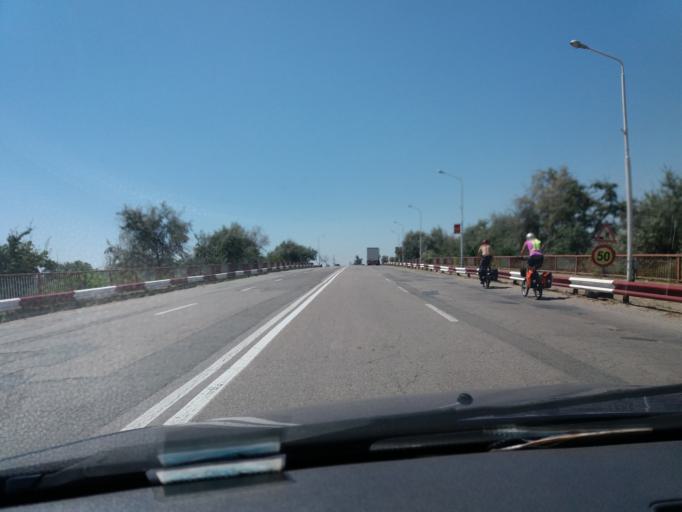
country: RO
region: Constanta
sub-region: Comuna Navodari
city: Navodari
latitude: 44.3241
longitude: 28.6235
